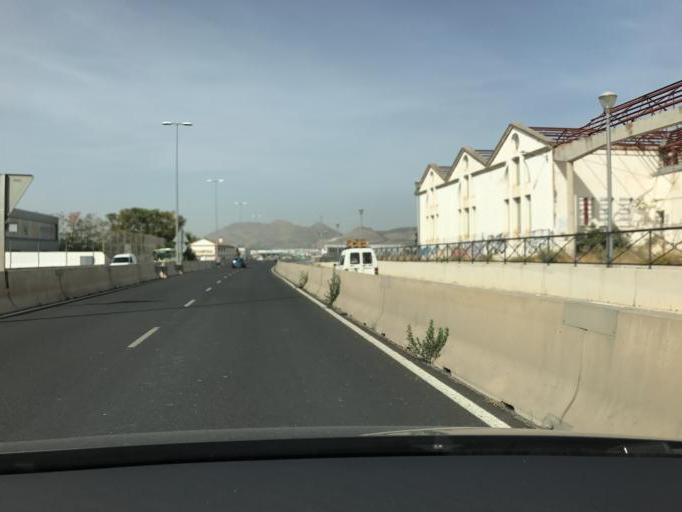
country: ES
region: Andalusia
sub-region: Provincia de Granada
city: Maracena
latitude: 37.1999
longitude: -3.6501
